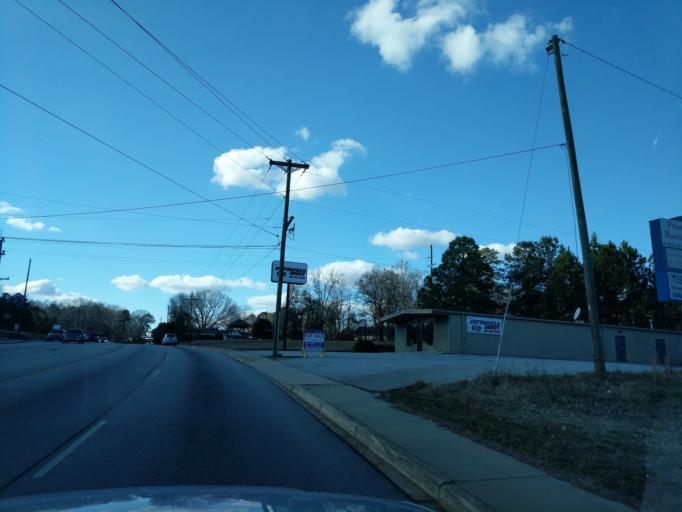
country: US
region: South Carolina
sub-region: Greenwood County
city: Greenwood
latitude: 34.2059
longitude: -82.1378
